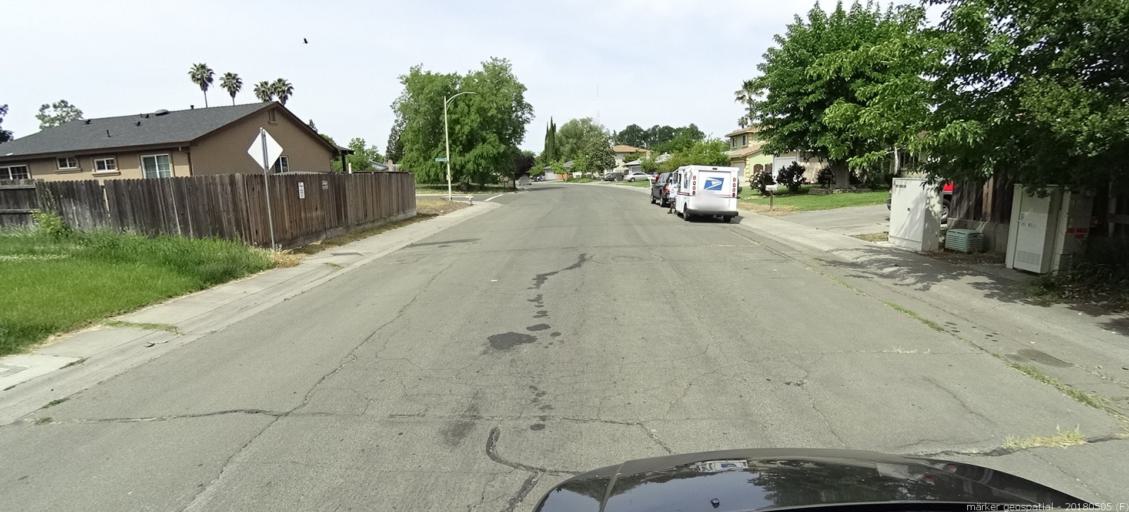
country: US
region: California
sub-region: Sacramento County
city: Rio Linda
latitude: 38.6478
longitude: -121.4660
